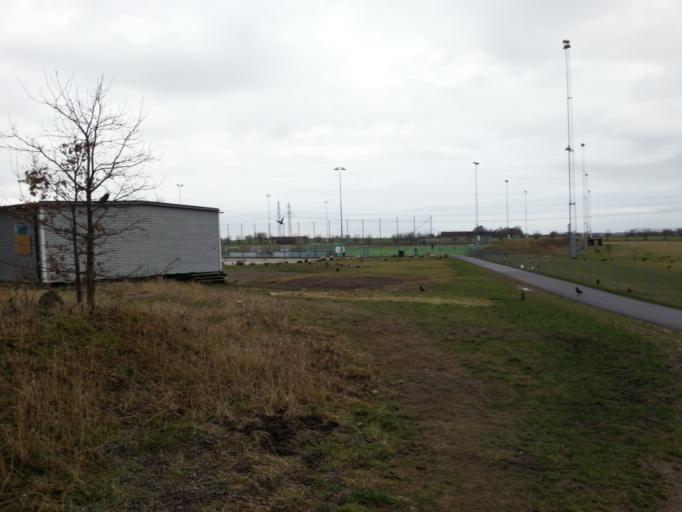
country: SE
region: Skane
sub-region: Lunds Kommun
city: Lund
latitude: 55.7288
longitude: 13.1543
